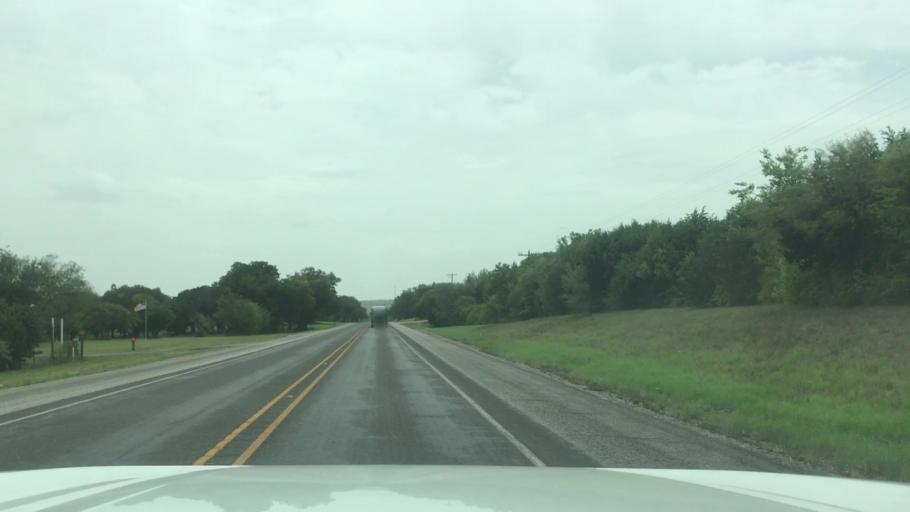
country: US
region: Texas
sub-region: Bosque County
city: Meridian
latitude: 31.8949
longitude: -97.6474
